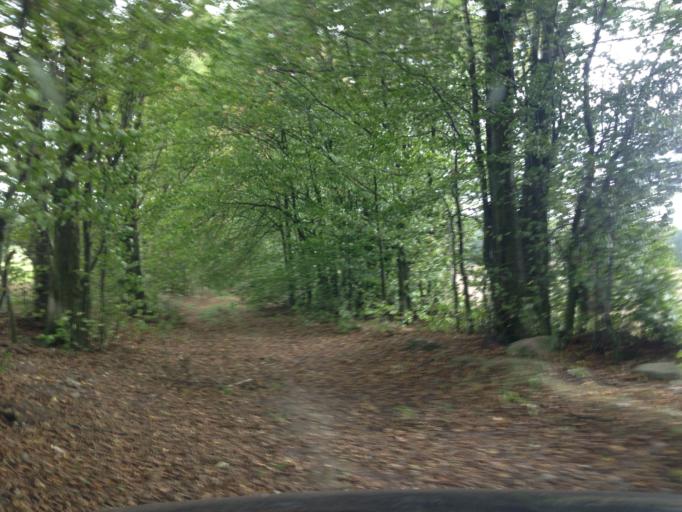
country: PL
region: Warmian-Masurian Voivodeship
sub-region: Powiat dzialdowski
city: Lidzbark
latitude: 53.2573
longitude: 19.7632
